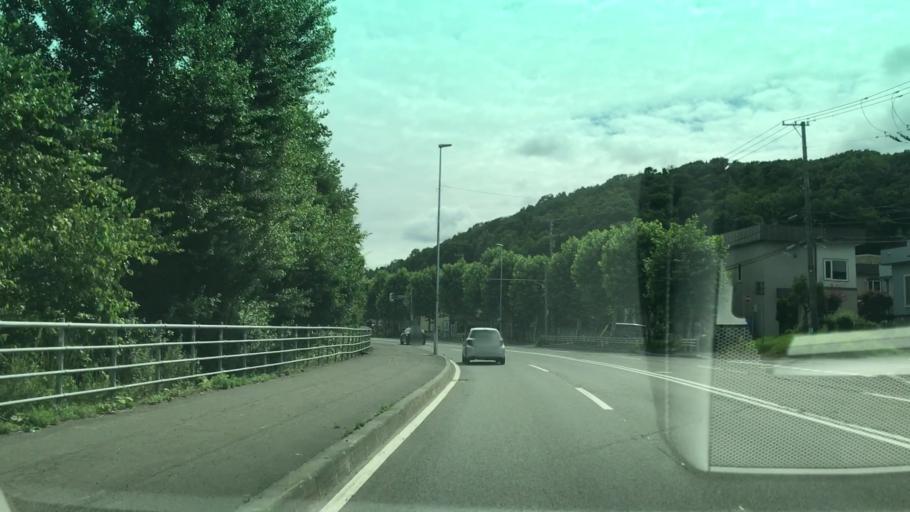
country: JP
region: Hokkaido
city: Sapporo
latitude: 42.9865
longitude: 141.3487
